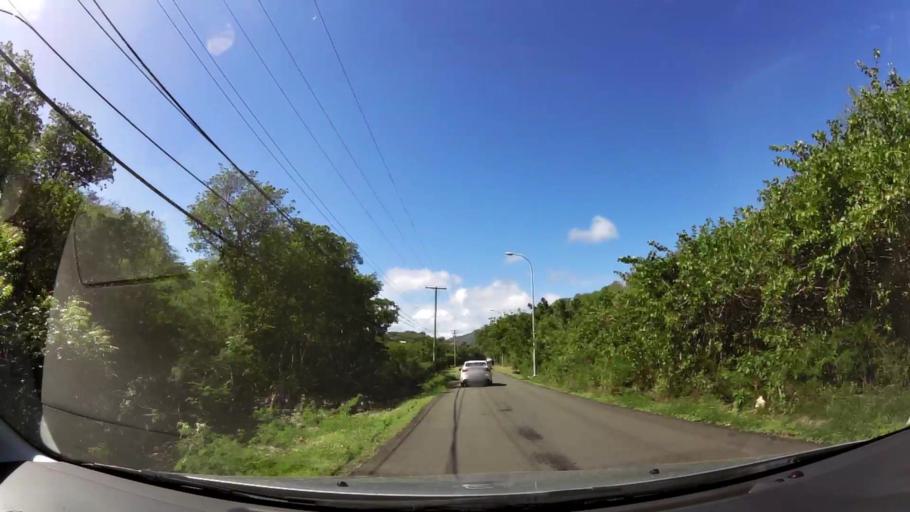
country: AG
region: Saint Paul
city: Falmouth
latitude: 17.0144
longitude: -61.7623
